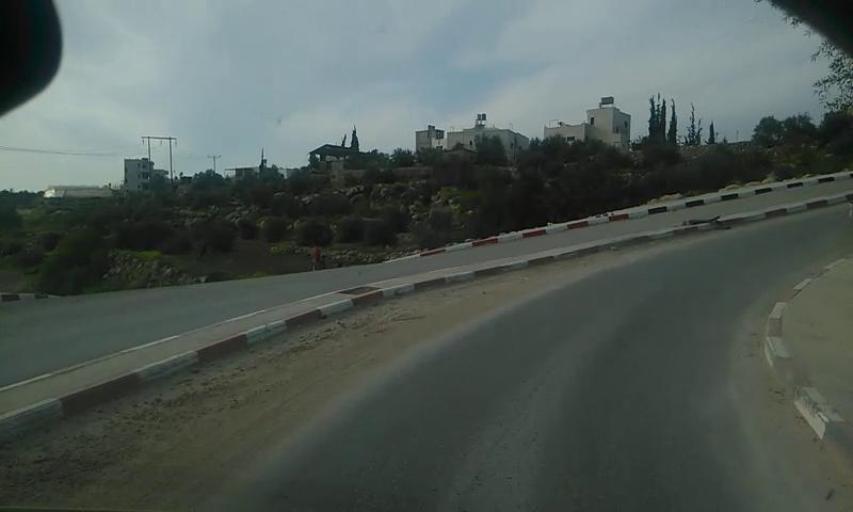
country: PS
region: West Bank
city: Bayt Ula
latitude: 31.5972
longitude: 35.0208
